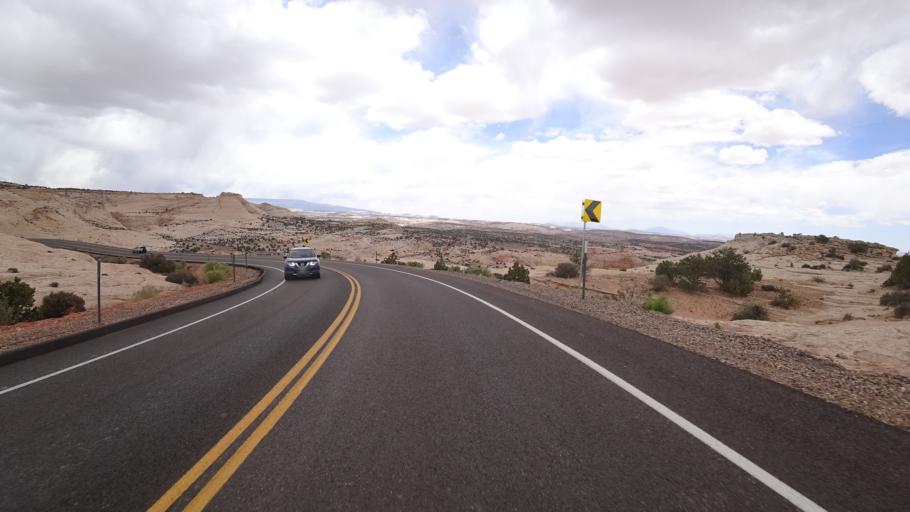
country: US
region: Utah
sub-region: Wayne County
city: Loa
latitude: 37.7431
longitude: -111.4474
